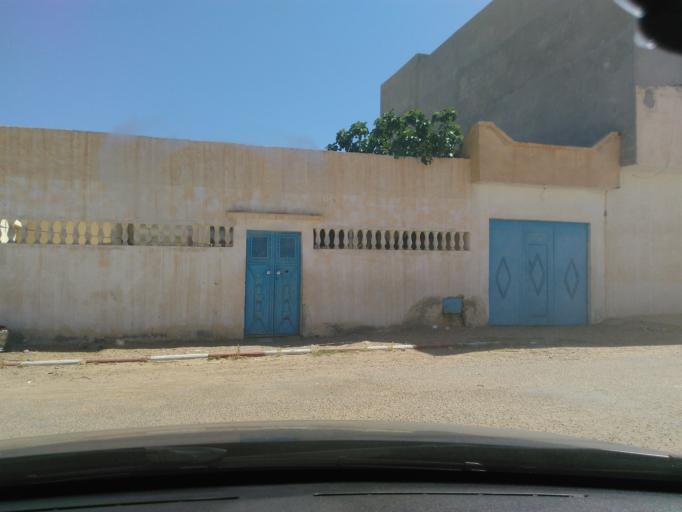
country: TN
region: Tataouine
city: Tataouine
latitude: 32.9449
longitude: 10.4611
